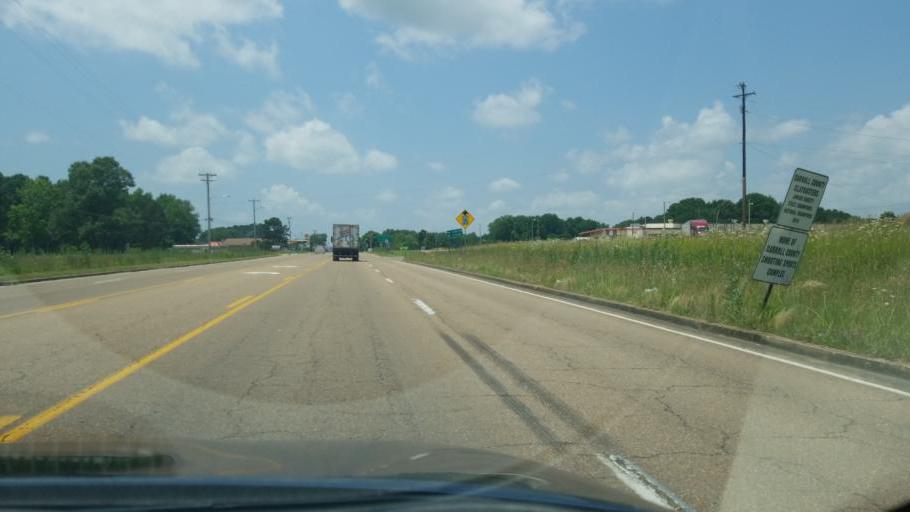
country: US
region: Tennessee
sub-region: Carroll County
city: Huntingdon
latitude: 36.0110
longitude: -88.3954
